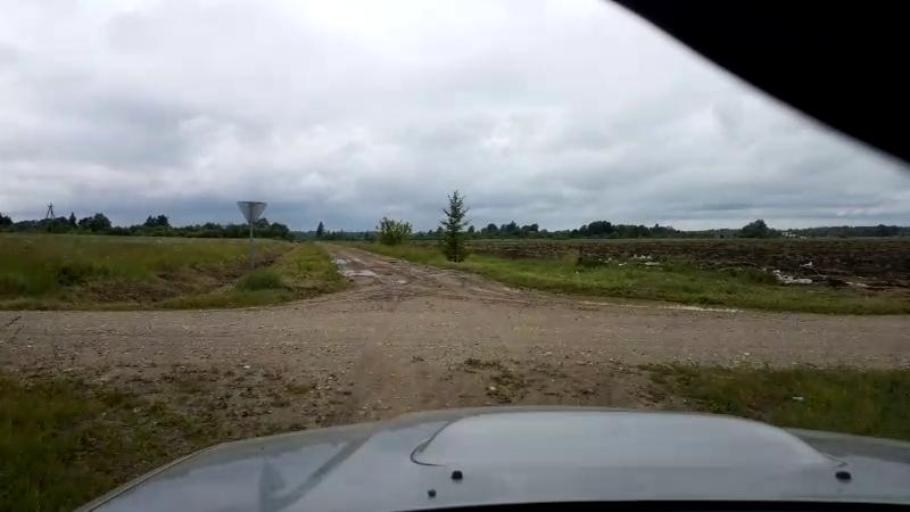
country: EE
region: Paernumaa
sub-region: Halinga vald
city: Parnu-Jaagupi
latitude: 58.5332
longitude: 24.5890
